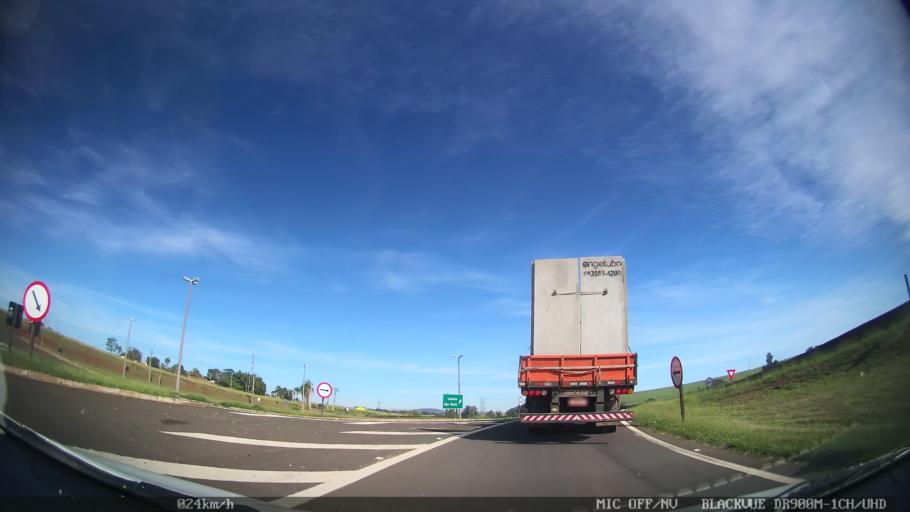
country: BR
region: Sao Paulo
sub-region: Araras
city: Araras
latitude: -22.3965
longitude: -47.3914
